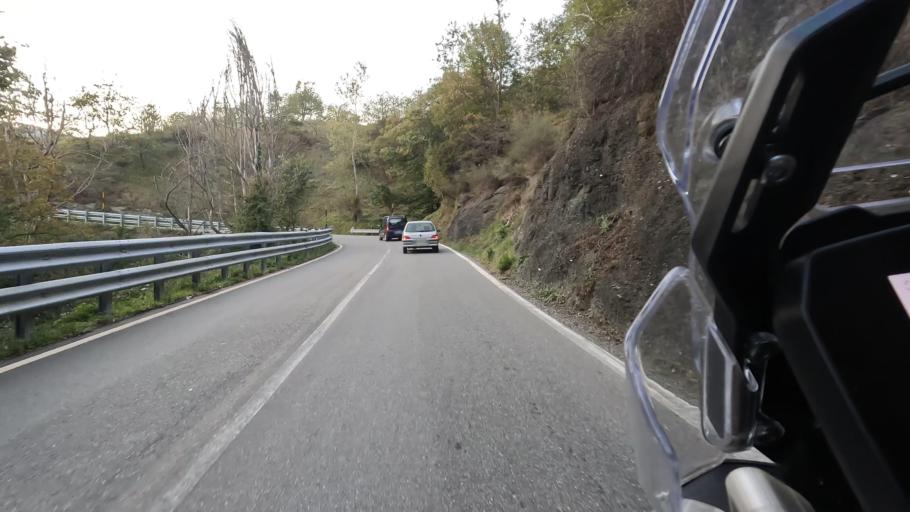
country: IT
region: Liguria
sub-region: Provincia di Savona
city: Osteria dei Cacciatori-Stella
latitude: 44.4217
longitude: 8.4765
